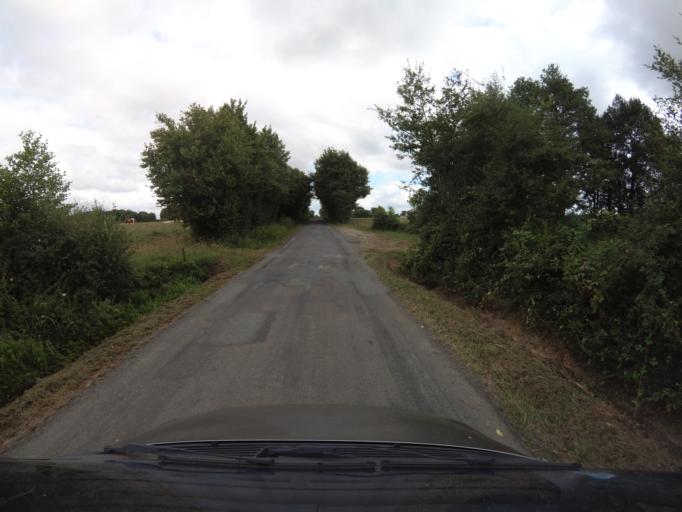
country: FR
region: Pays de la Loire
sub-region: Departement de la Vendee
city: Saint-Philbert-de-Bouaine
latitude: 47.0172
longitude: -1.5530
